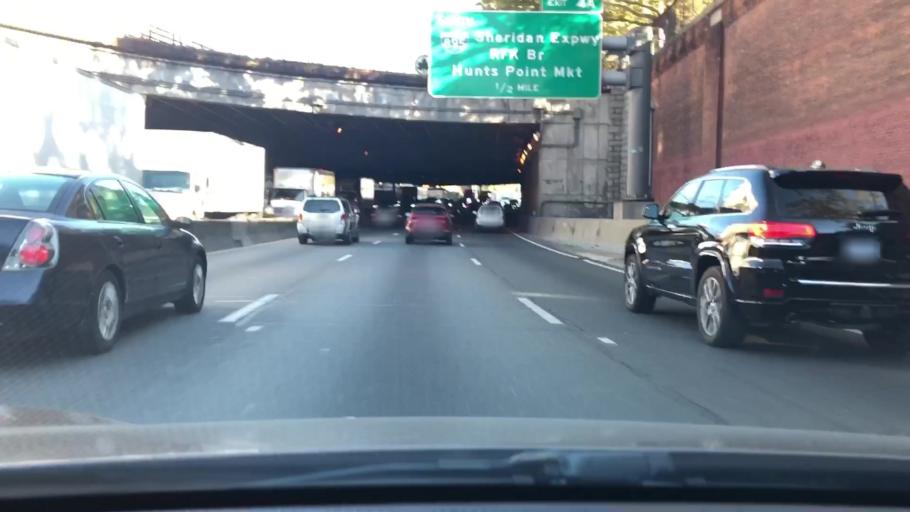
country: US
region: New York
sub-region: Bronx
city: The Bronx
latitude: 40.8434
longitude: -73.8925
